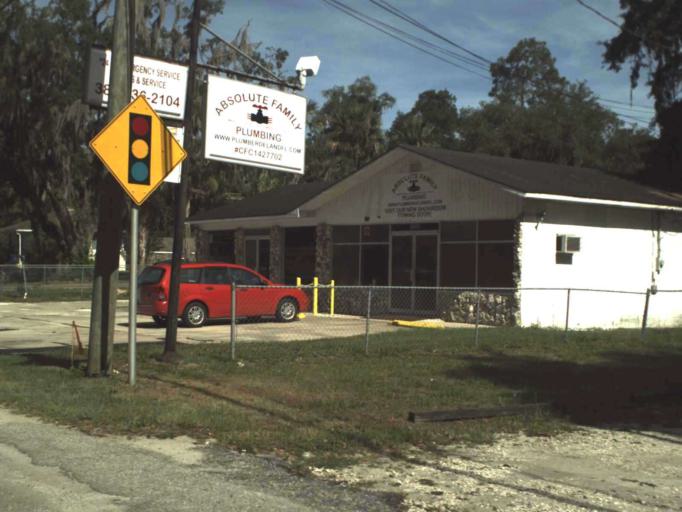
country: US
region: Florida
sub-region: Volusia County
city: DeLand
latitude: 29.0282
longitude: -81.2770
